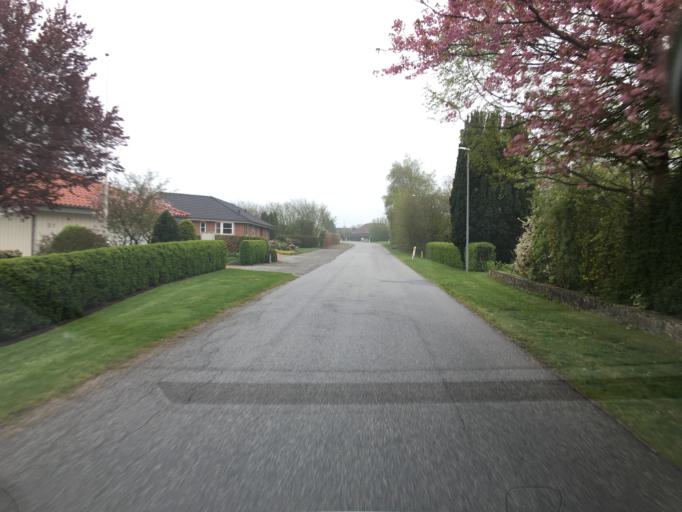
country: DK
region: South Denmark
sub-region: Haderslev Kommune
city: Haderslev
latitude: 55.2860
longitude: 9.4545
